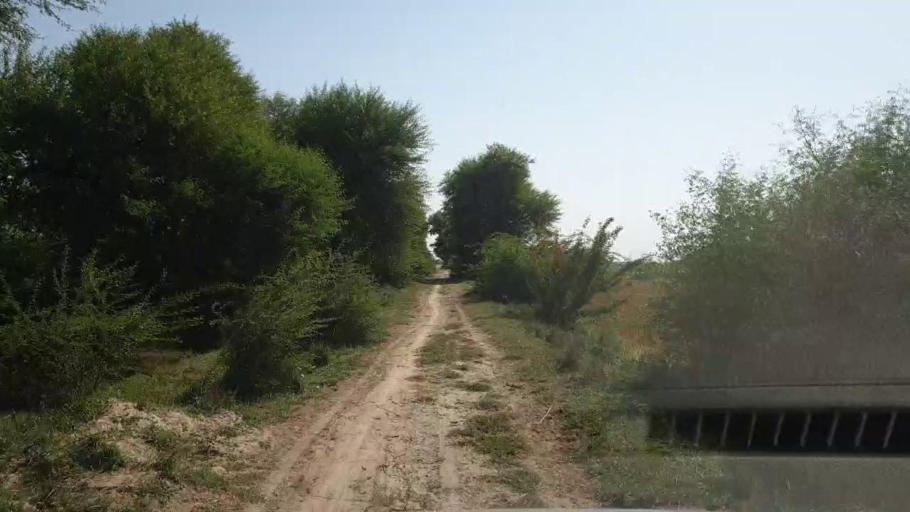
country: PK
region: Sindh
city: Kadhan
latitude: 24.6266
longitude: 68.9942
